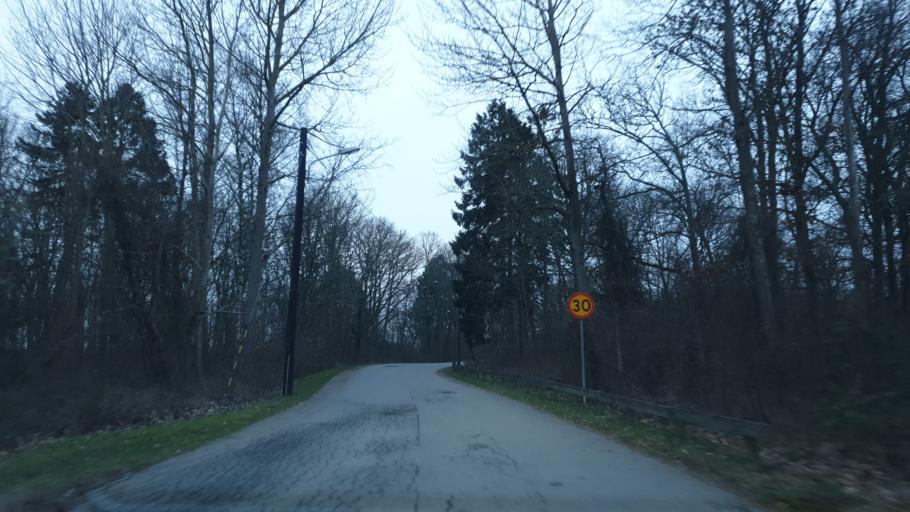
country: SE
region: Blekinge
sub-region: Karlskrona Kommun
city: Karlskrona
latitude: 56.1720
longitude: 15.5667
